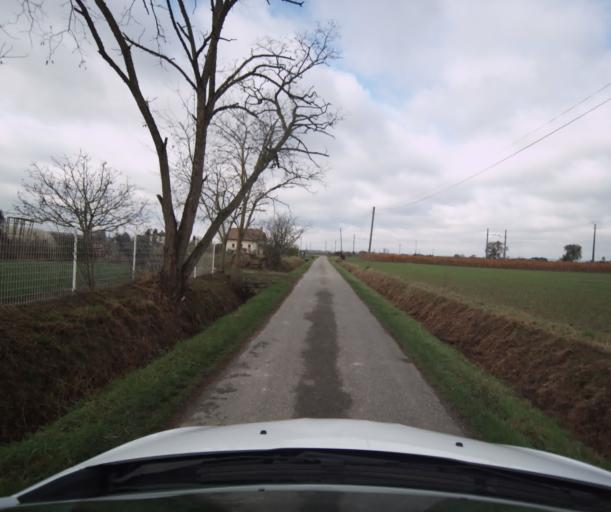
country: FR
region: Midi-Pyrenees
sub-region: Departement du Tarn-et-Garonne
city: Castelsarrasin
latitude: 44.0354
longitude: 1.1422
